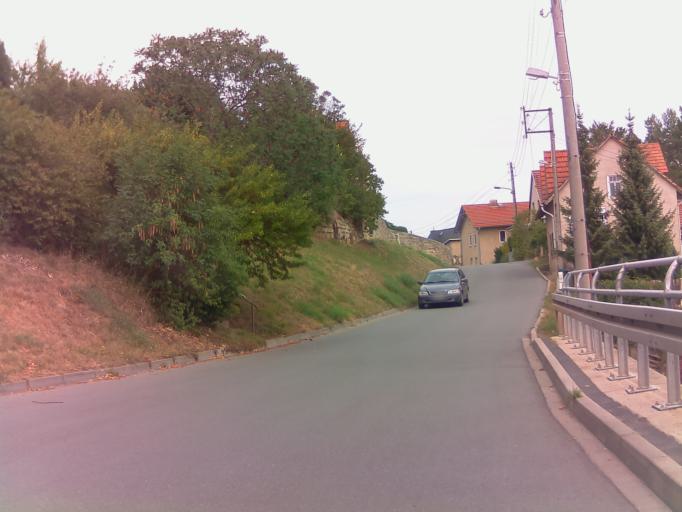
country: DE
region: Thuringia
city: Orlamunde
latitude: 50.7724
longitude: 11.5151
